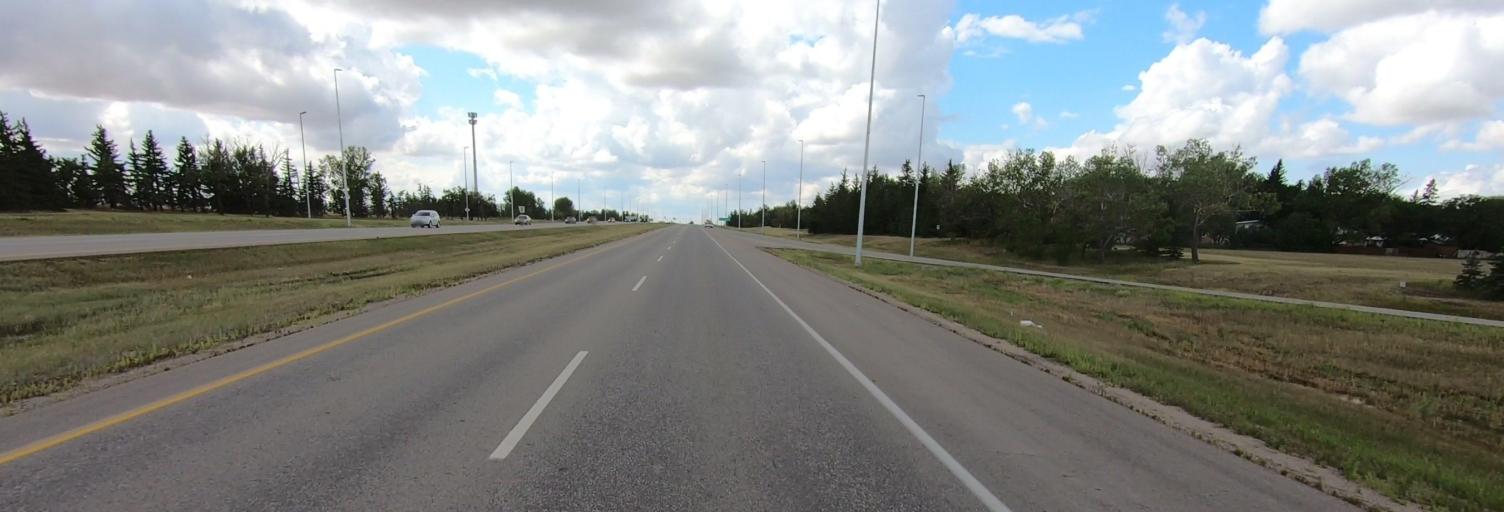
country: CA
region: Saskatchewan
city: Regina
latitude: 50.4057
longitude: -104.5920
